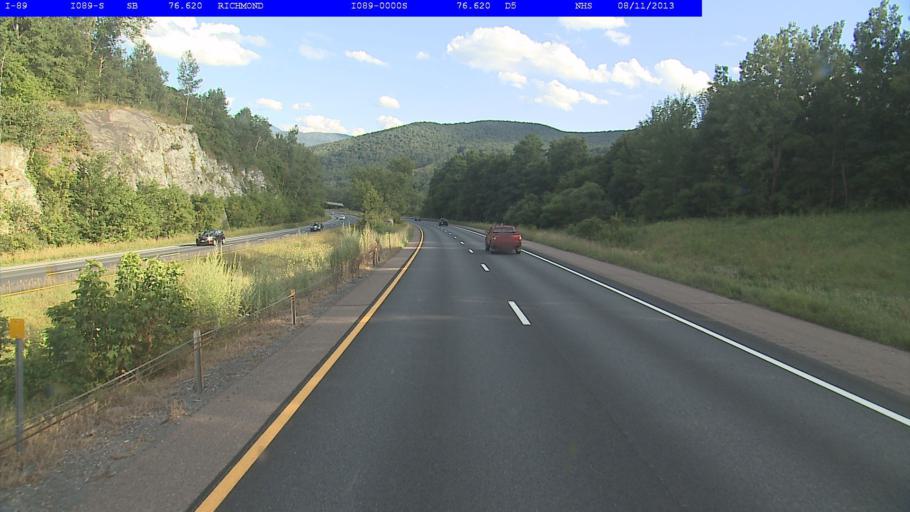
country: US
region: Vermont
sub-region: Chittenden County
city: Williston
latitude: 44.4051
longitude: -72.9892
